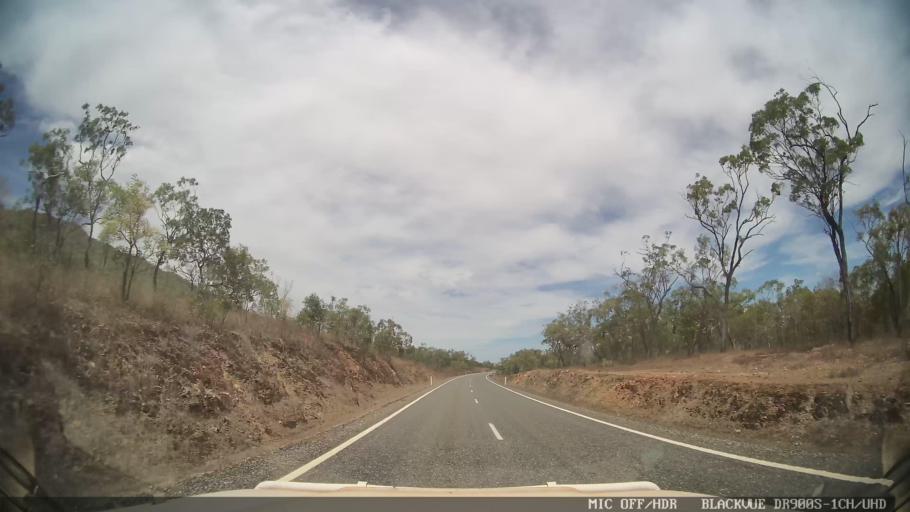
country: AU
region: Queensland
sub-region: Cairns
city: Port Douglas
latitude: -16.3645
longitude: 144.7317
